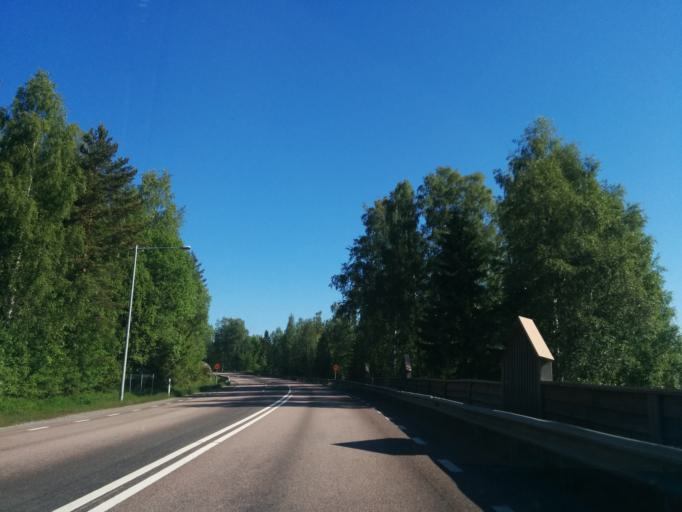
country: SE
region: Vaesternorrland
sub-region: Kramfors Kommun
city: Kramfors
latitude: 62.8098
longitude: 17.8683
